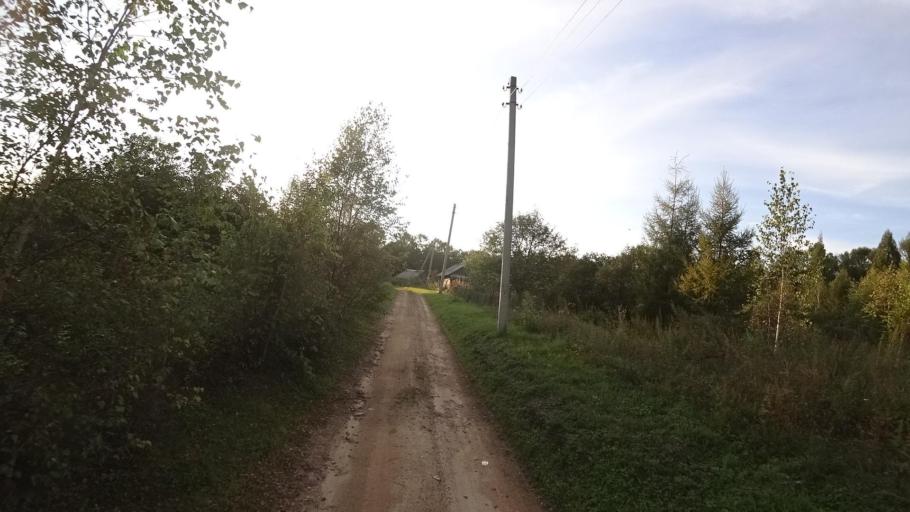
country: RU
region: Jewish Autonomous Oblast
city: Kul'dur
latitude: 49.2097
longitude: 131.6480
